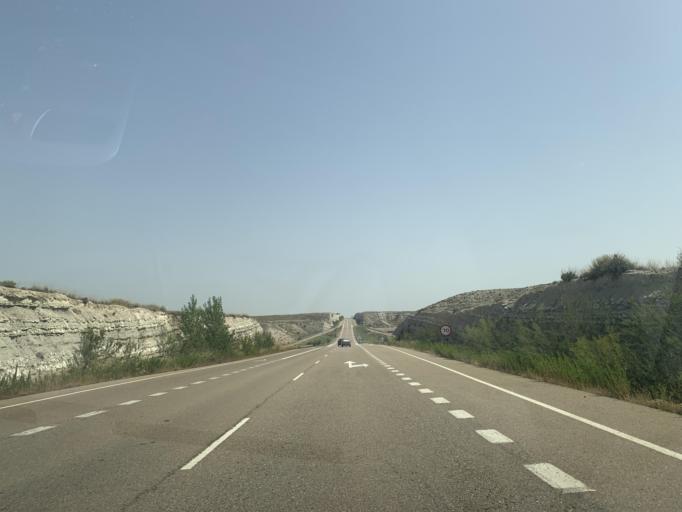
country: ES
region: Aragon
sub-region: Provincia de Zaragoza
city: Fuentes de Ebro
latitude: 41.4725
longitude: -0.7189
